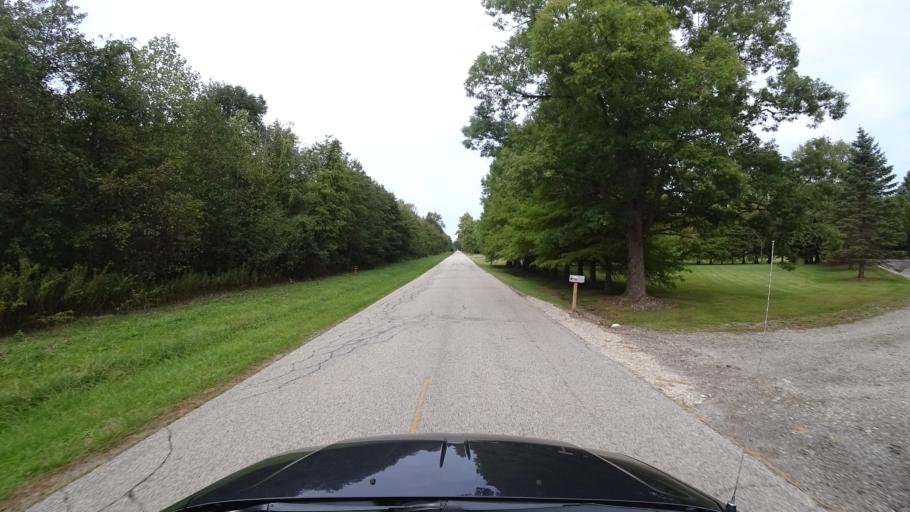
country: US
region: Indiana
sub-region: LaPorte County
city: Long Beach
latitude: 41.7324
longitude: -86.8162
